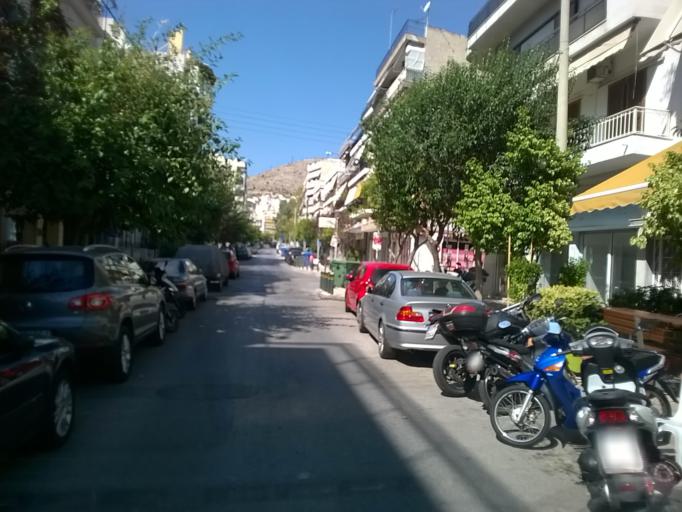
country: GR
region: Attica
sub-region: Nomos Piraios
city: Keratsini
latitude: 37.9701
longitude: 23.6244
